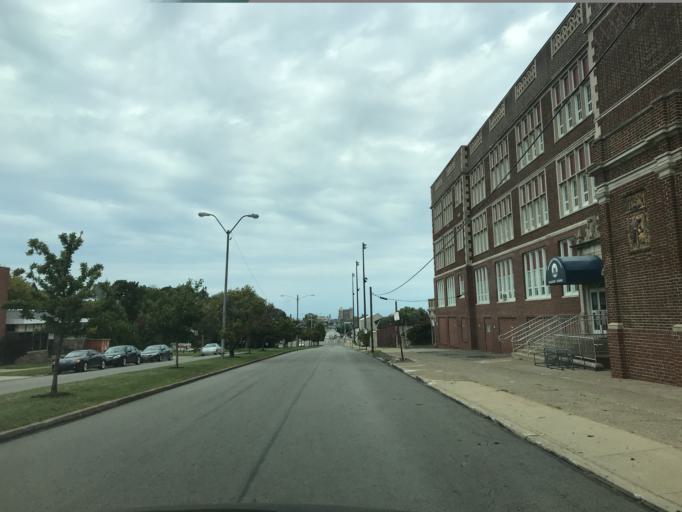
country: US
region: Pennsylvania
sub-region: Erie County
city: Erie
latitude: 42.1094
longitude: -80.0718
